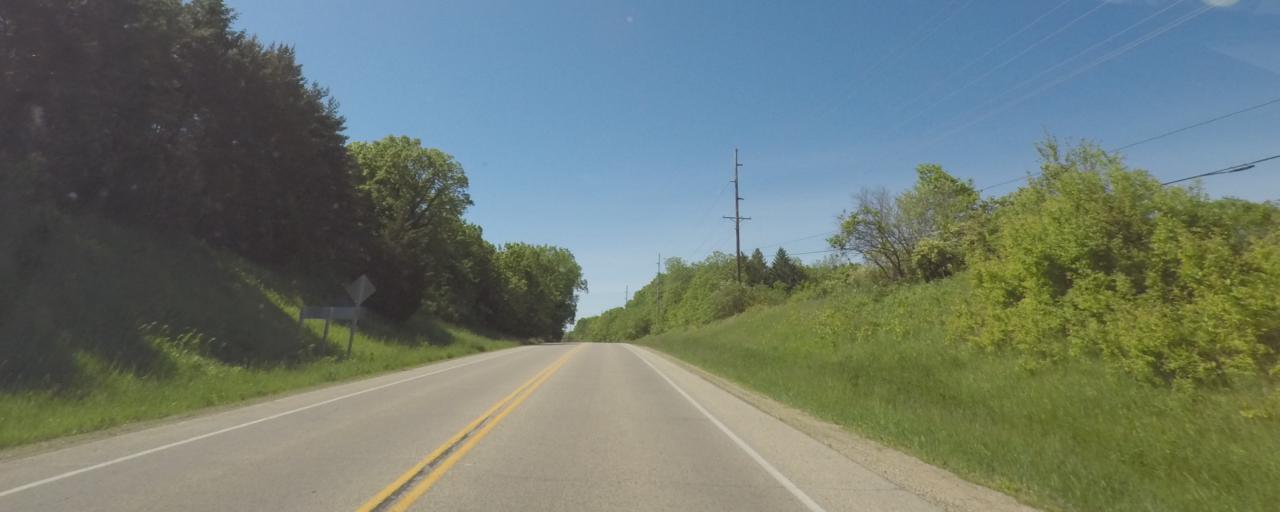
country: US
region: Wisconsin
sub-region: Green County
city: Brooklyn
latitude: 42.8799
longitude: -89.3689
